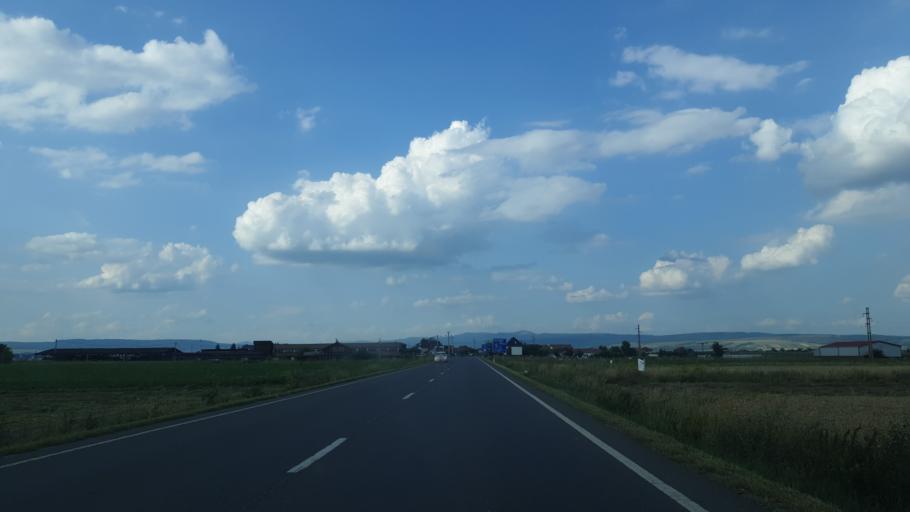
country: RO
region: Covasna
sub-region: Municipiul Sfantu Gheorghe
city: Sfantu-Gheorghe
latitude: 45.8287
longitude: 25.8025
